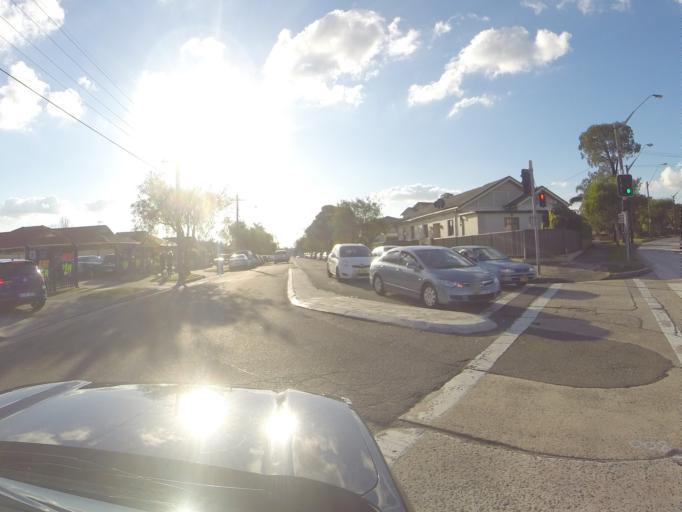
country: AU
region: New South Wales
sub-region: Rockdale
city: Bexley
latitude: -33.9543
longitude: 151.1190
